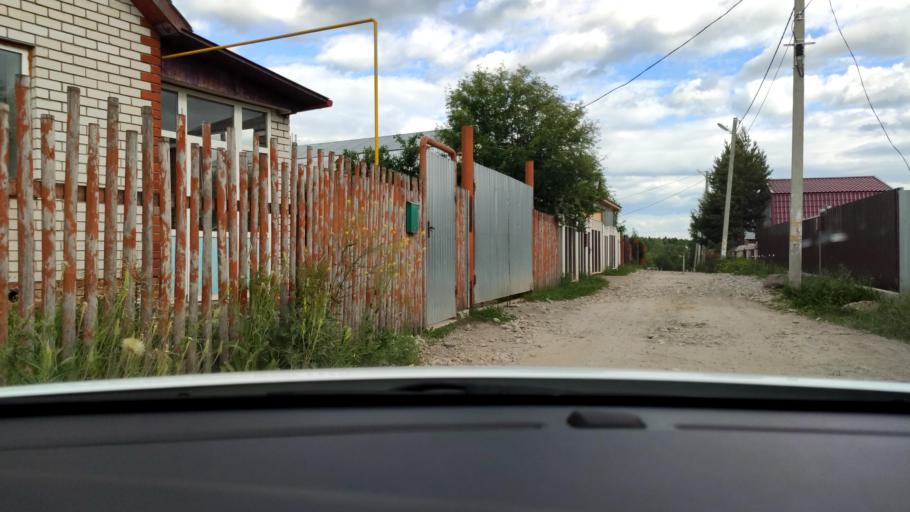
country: RU
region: Tatarstan
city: Stolbishchi
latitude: 55.7603
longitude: 49.3023
